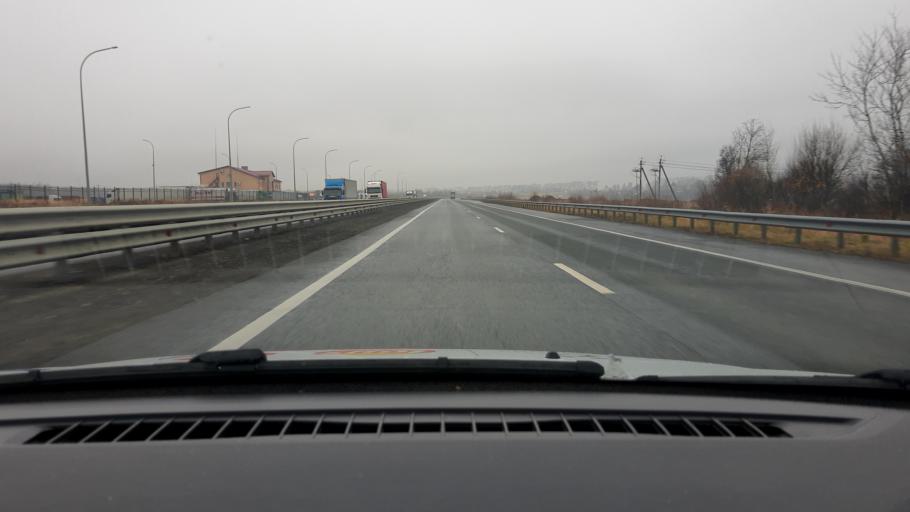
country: RU
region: Nizjnij Novgorod
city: Burevestnik
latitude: 56.1412
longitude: 43.7612
